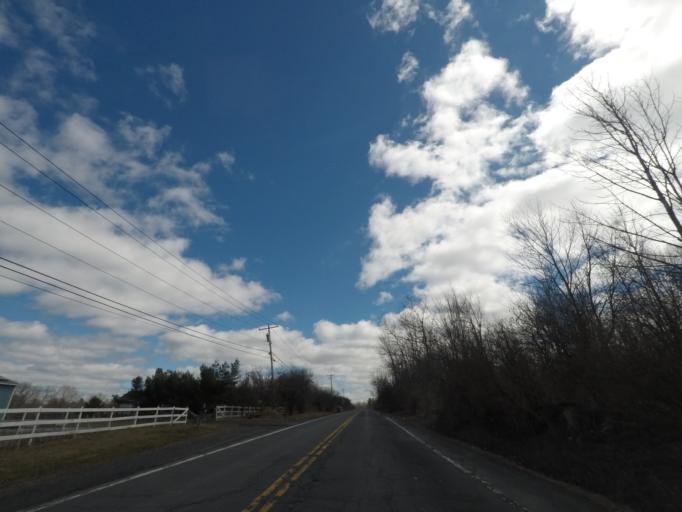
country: US
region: New York
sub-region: Albany County
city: Altamont
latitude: 42.6748
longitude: -74.0735
